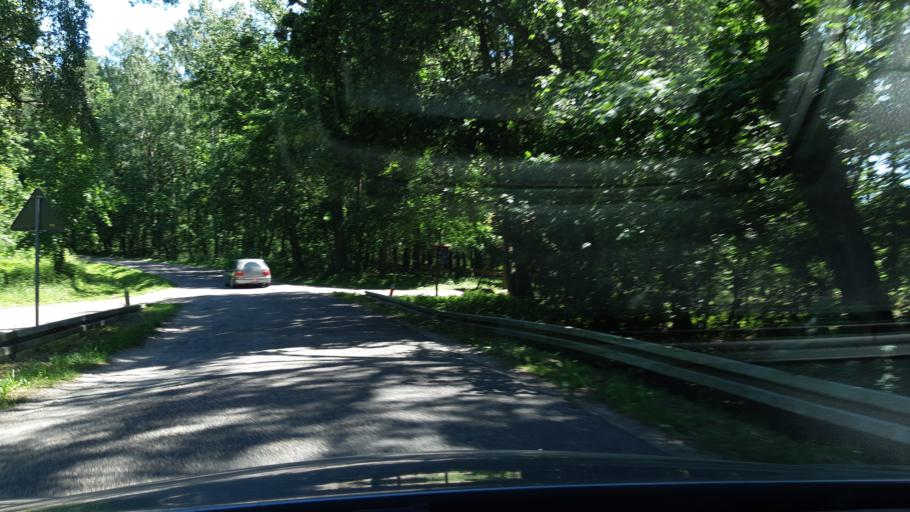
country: PL
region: Warmian-Masurian Voivodeship
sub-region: Powiat gizycki
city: Gizycko
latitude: 53.9459
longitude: 21.7476
